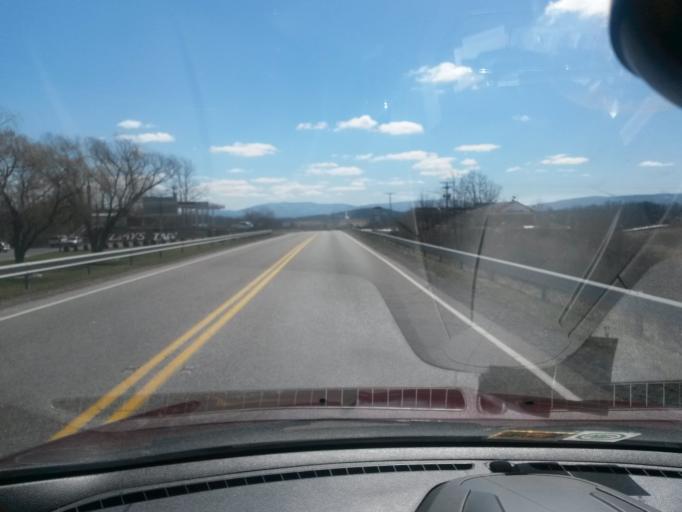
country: US
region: Virginia
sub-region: Augusta County
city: Jolivue
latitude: 38.0751
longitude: -79.0854
